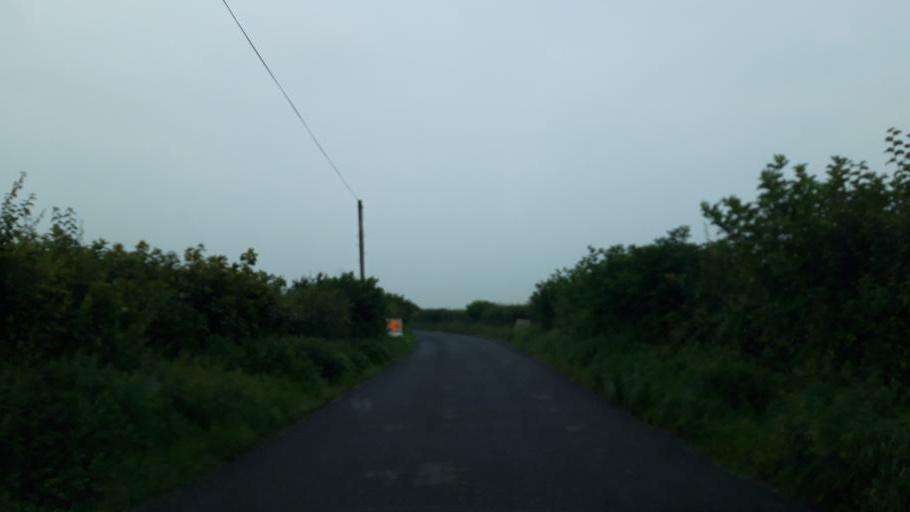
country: IE
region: Leinster
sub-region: Kilkenny
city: Thomastown
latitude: 52.6033
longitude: -7.1421
